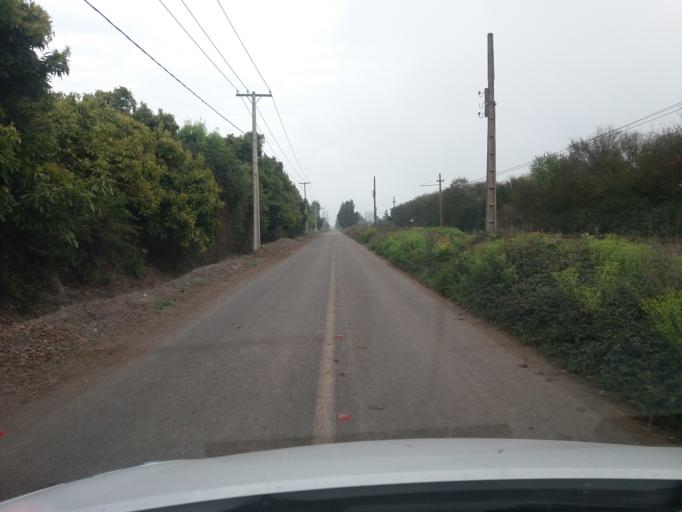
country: CL
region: Valparaiso
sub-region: Provincia de San Felipe
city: Llaillay
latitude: -32.8395
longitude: -71.0586
